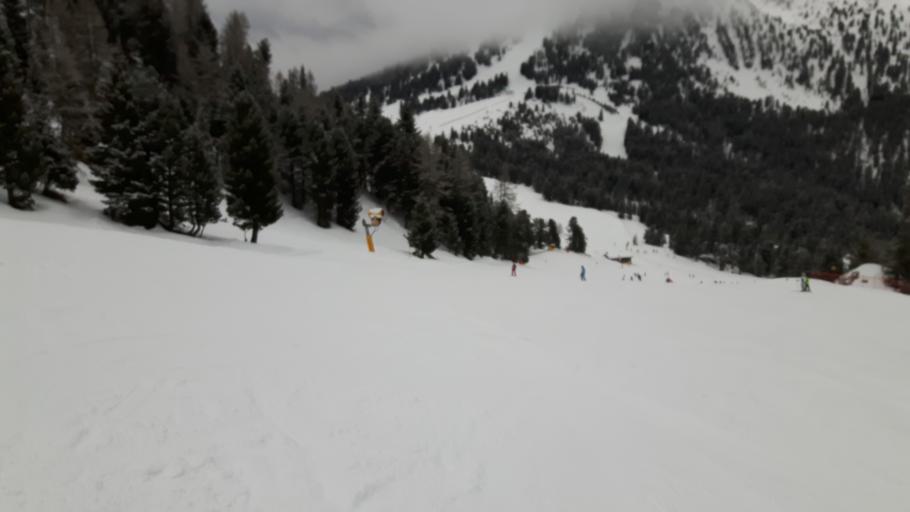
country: IT
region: Trentino-Alto Adige
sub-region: Bolzano
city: Nova Levante
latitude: 46.3607
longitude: 11.5438
